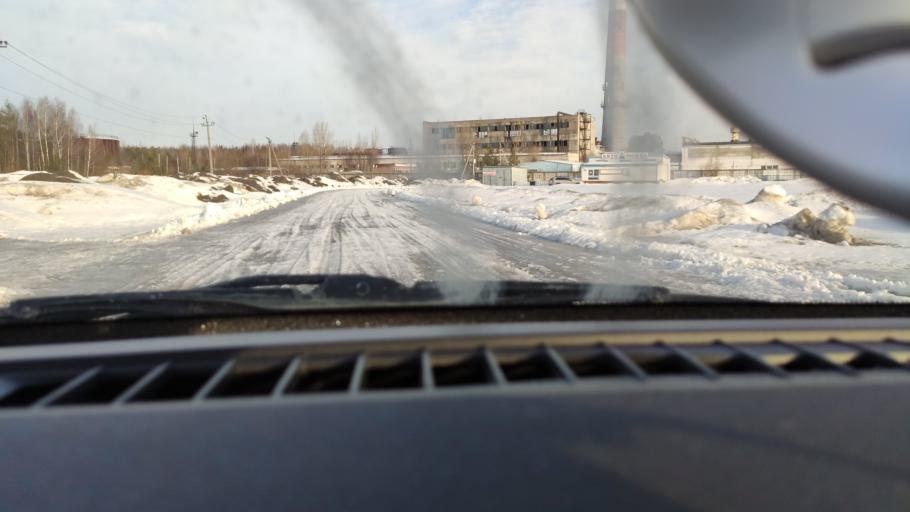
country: RU
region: Perm
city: Perm
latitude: 58.0378
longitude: 56.2028
